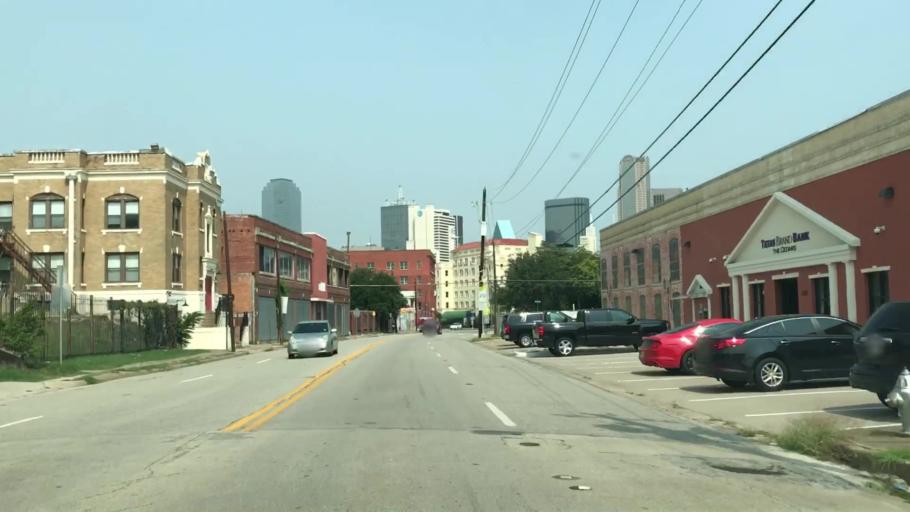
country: US
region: Texas
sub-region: Dallas County
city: Dallas
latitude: 32.7708
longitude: -96.7884
